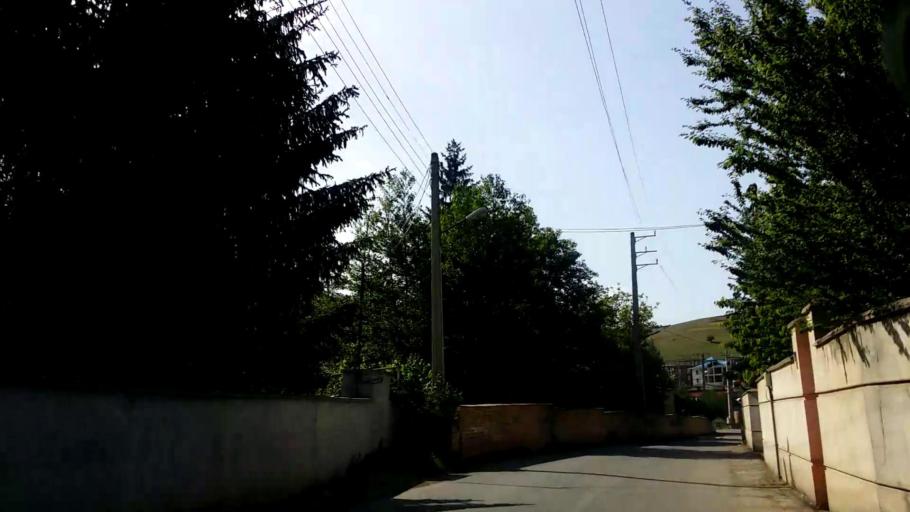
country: IR
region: Mazandaran
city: `Abbasabad
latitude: 36.5285
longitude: 51.1773
